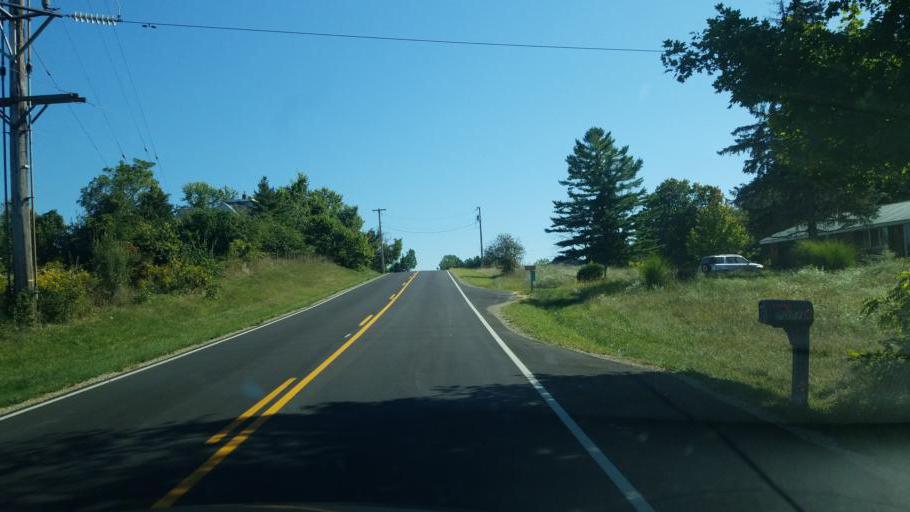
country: US
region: Ohio
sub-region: Champaign County
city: North Lewisburg
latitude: 40.1613
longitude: -83.6036
